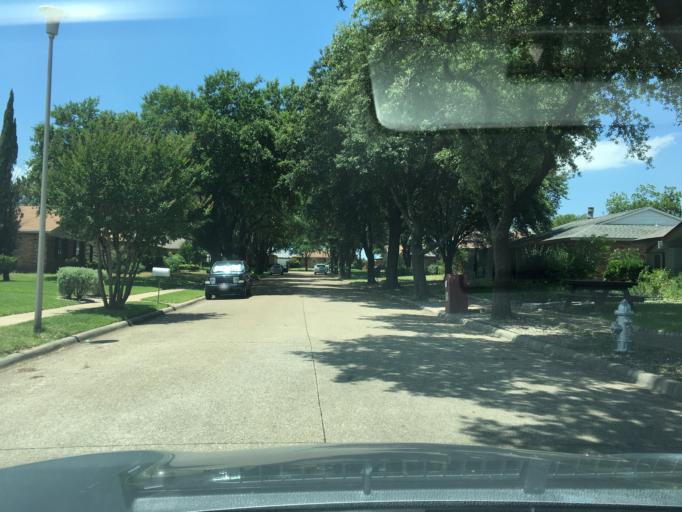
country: US
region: Texas
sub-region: Dallas County
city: Garland
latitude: 32.9523
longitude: -96.6750
